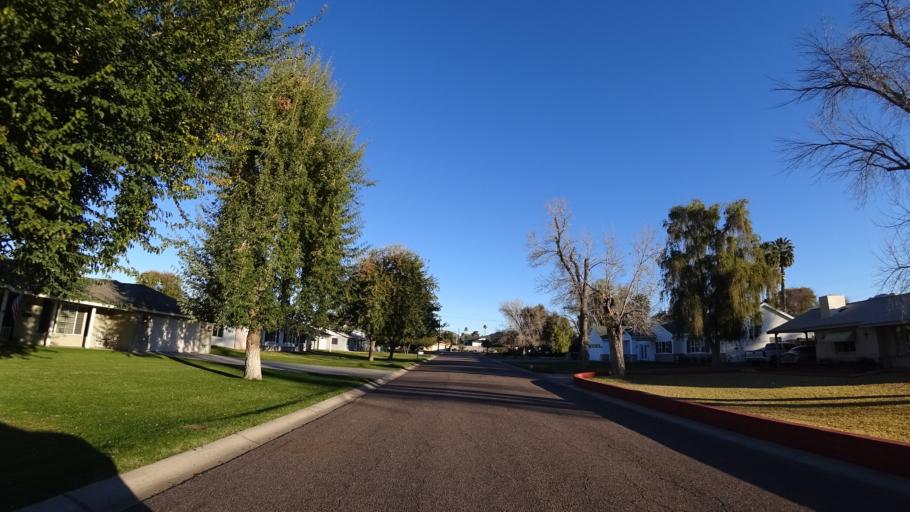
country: US
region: Arizona
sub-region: Maricopa County
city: Paradise Valley
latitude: 33.4906
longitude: -112.0075
